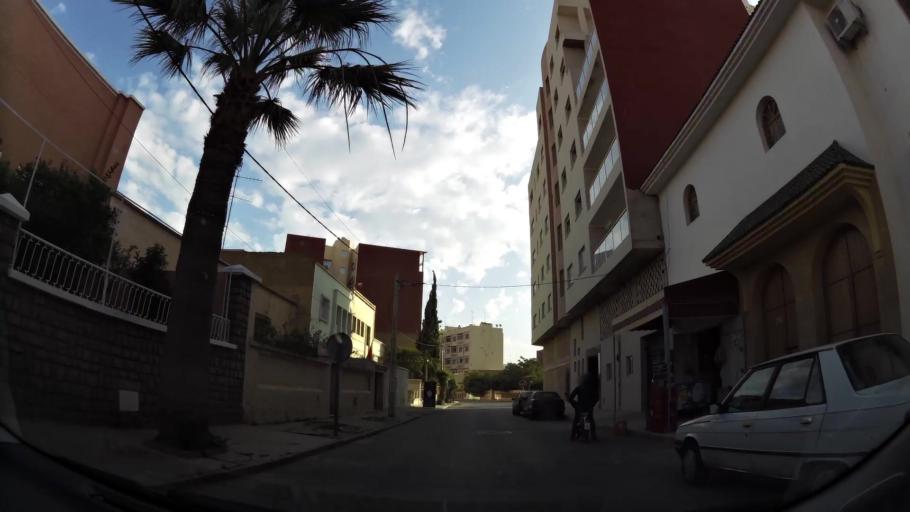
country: MA
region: Oriental
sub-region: Oujda-Angad
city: Oujda
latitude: 34.6793
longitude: -1.9225
